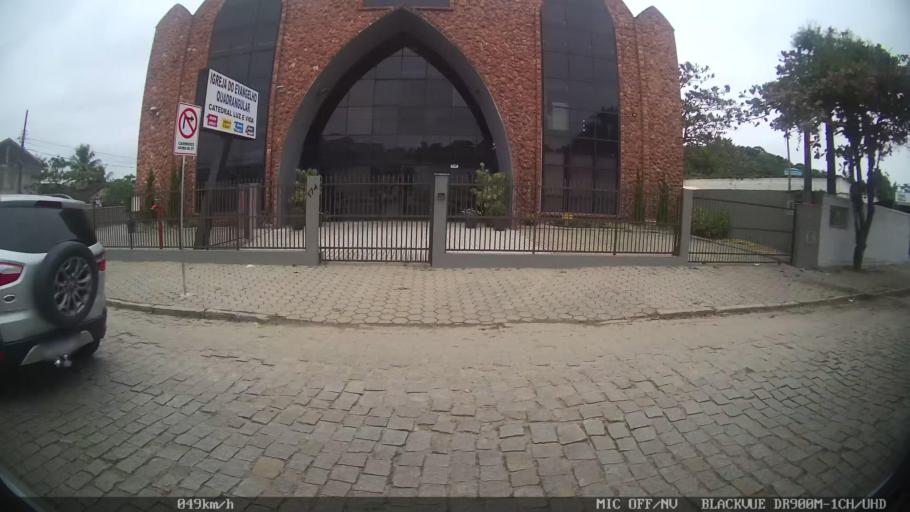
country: BR
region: Santa Catarina
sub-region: Joinville
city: Joinville
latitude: -26.3437
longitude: -48.8552
